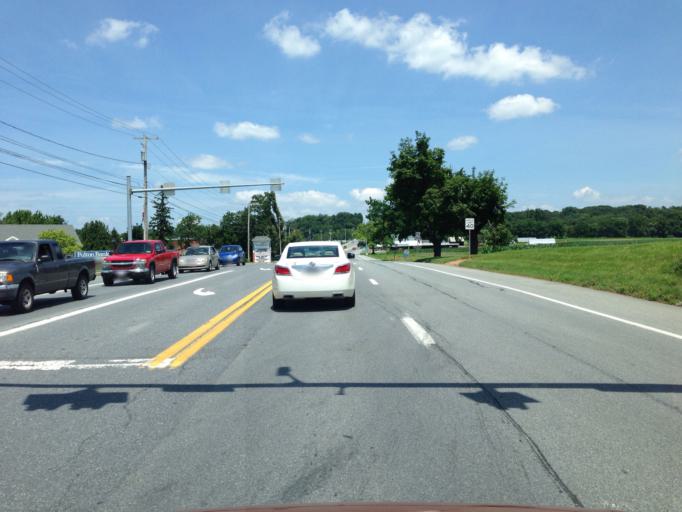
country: US
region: Pennsylvania
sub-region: Lancaster County
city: Lititz
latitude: 40.1266
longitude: -76.3050
